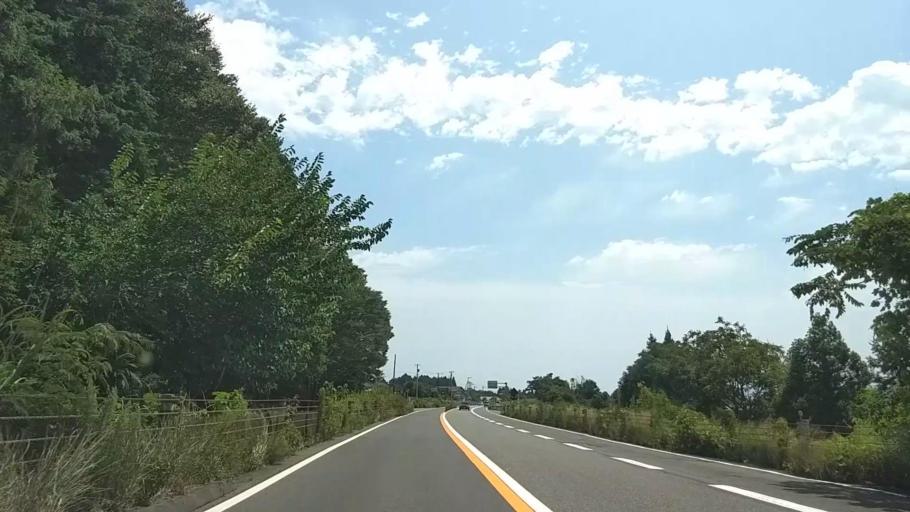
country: JP
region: Shizuoka
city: Fujinomiya
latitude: 35.2873
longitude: 138.6116
